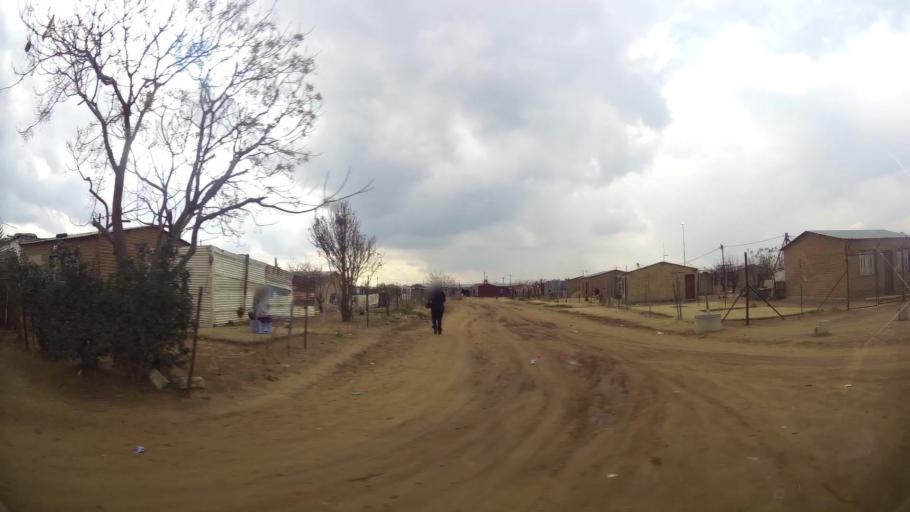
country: ZA
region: Orange Free State
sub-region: Fezile Dabi District Municipality
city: Sasolburg
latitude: -26.8622
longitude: 27.8744
